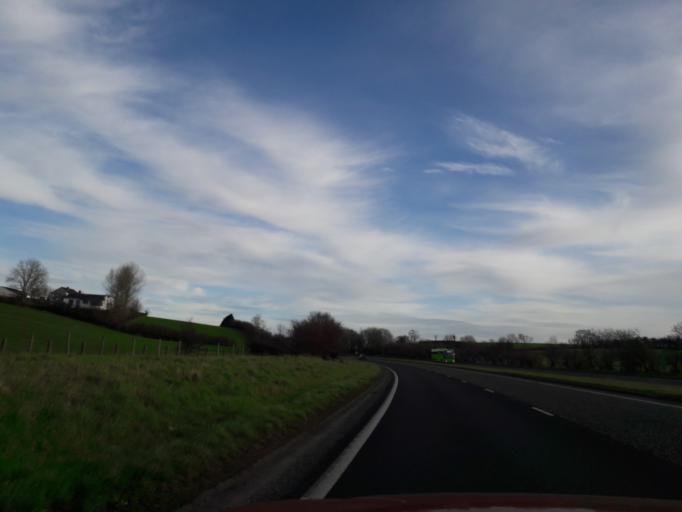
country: GB
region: Northern Ireland
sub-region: Banbridge District
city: Banbridge
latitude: 54.3474
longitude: -6.2443
